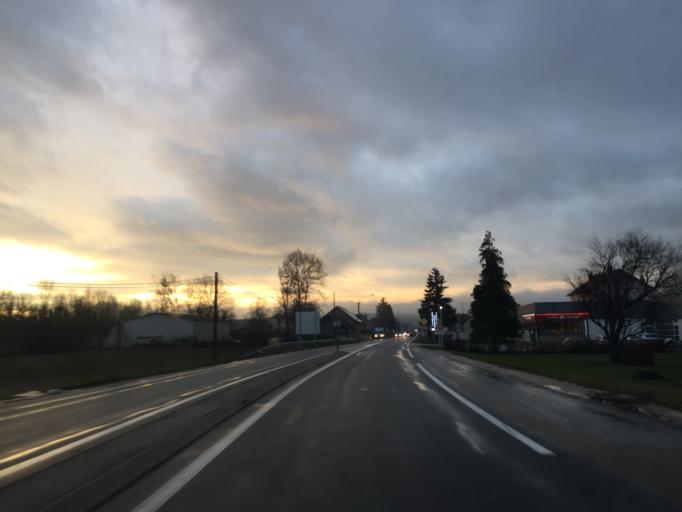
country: FR
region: Franche-Comte
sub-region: Departement du Jura
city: Choisey
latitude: 47.0257
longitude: 5.4949
